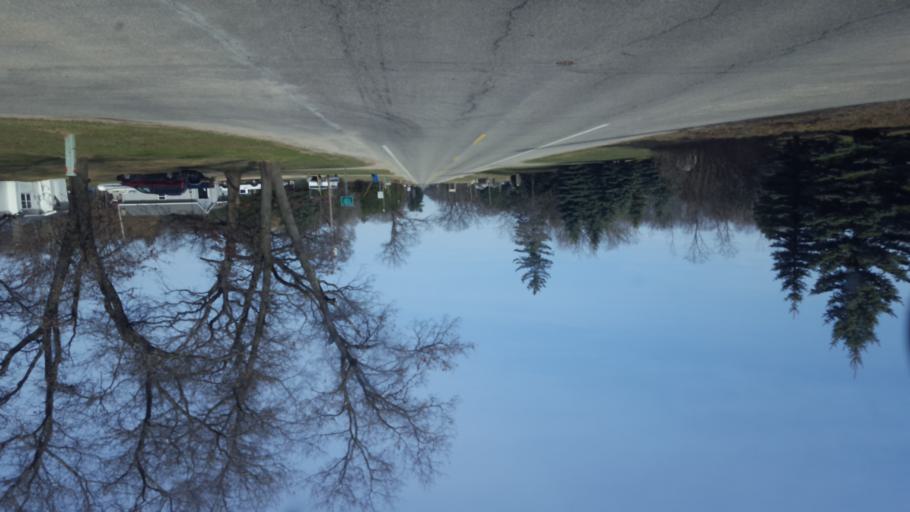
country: US
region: Michigan
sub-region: Newaygo County
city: White Cloud
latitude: 43.5550
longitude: -85.6815
